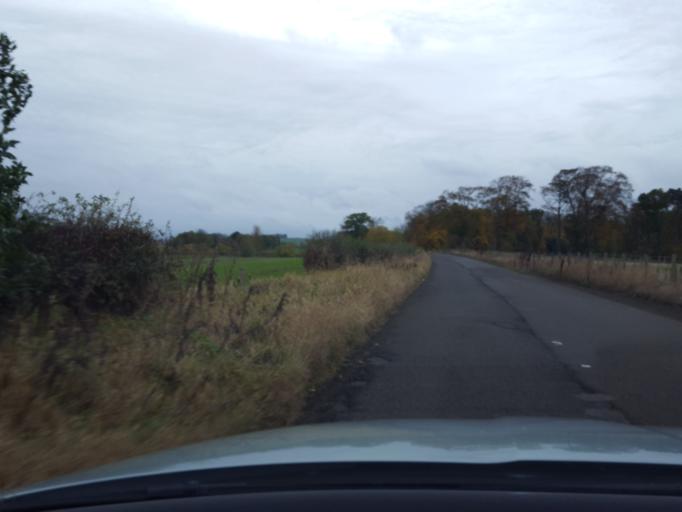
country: GB
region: Scotland
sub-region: Edinburgh
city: Ratho
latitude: 55.9207
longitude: -3.3468
